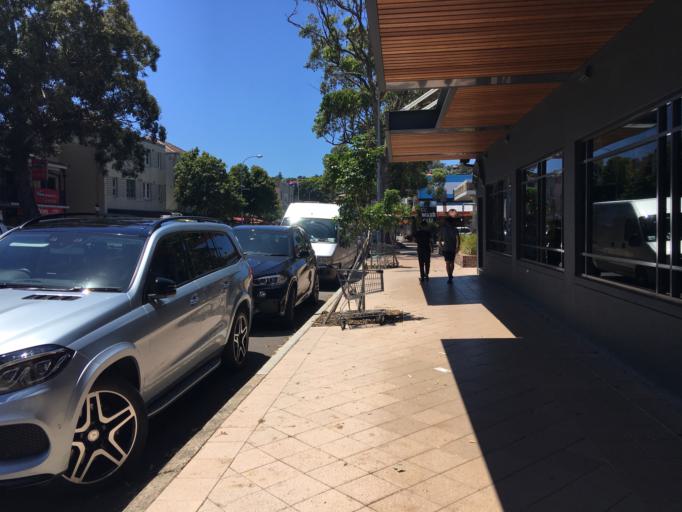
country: AU
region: New South Wales
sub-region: Waverley
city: Dover Heights
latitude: -33.8708
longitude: 151.2682
